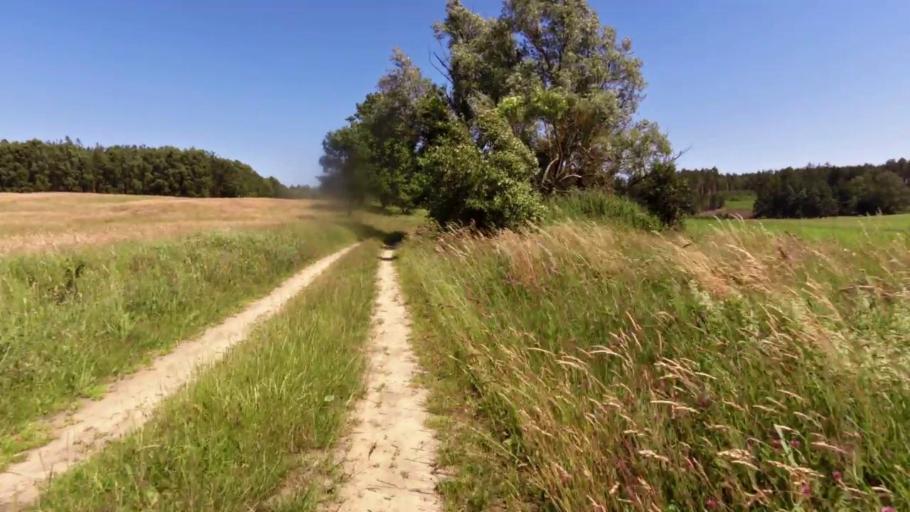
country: PL
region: West Pomeranian Voivodeship
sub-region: Powiat swidwinski
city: Polczyn-Zdroj
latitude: 53.8997
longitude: 16.0970
